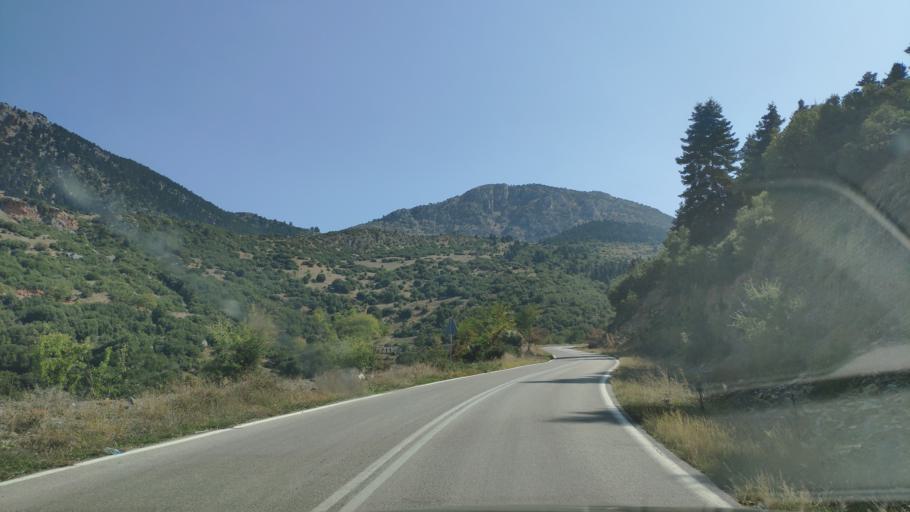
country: GR
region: West Greece
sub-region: Nomos Achaias
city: Aiyira
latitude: 37.9216
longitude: 22.3347
